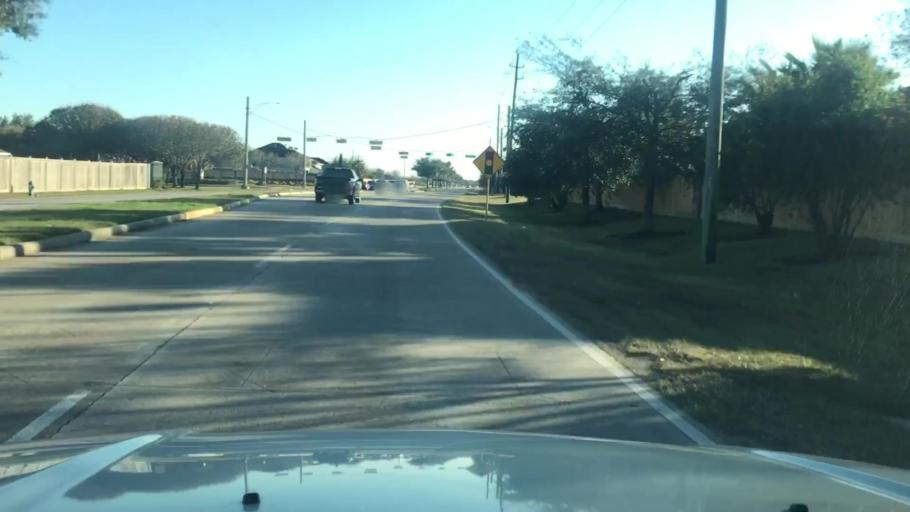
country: US
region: Texas
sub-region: Fort Bend County
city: Cinco Ranch
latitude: 29.8433
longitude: -95.7190
